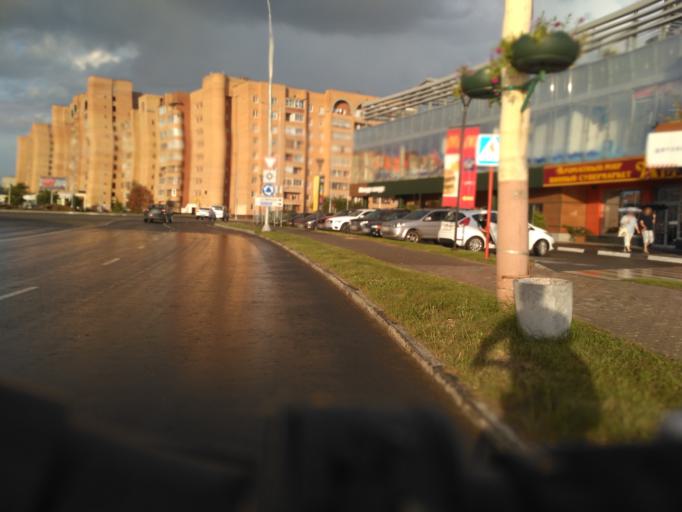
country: RU
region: Moskovskaya
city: Dubna
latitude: 56.7359
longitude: 37.1611
